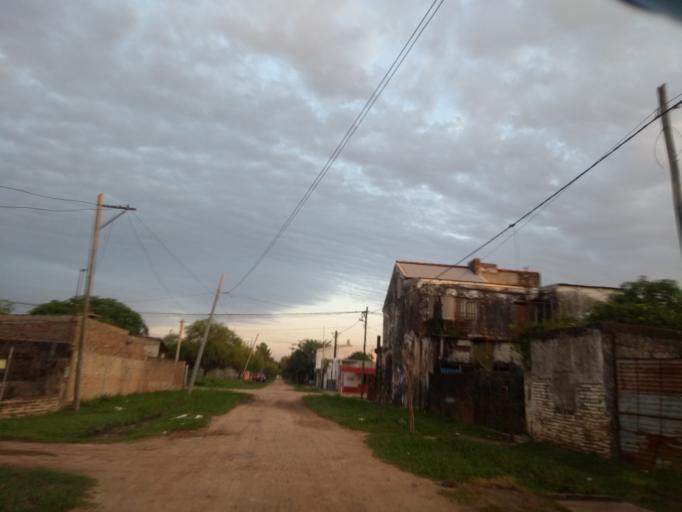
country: AR
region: Chaco
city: Resistencia
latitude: -27.4759
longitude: -58.9774
